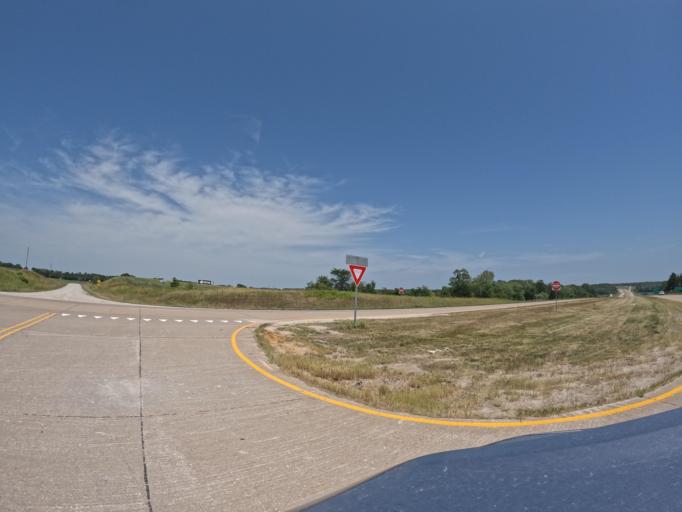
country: US
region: Iowa
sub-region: Henry County
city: Mount Pleasant
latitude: 40.9746
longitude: -91.6598
